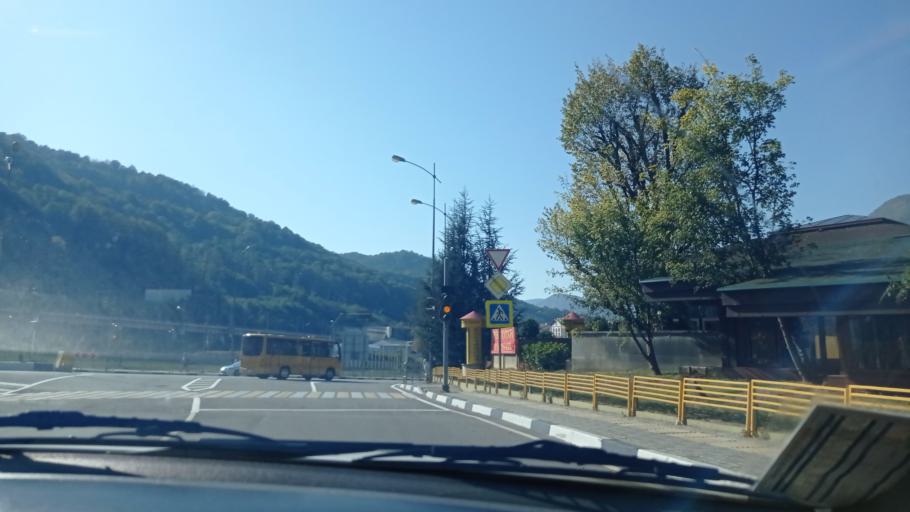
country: RU
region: Krasnodarskiy
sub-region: Sochi City
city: Krasnaya Polyana
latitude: 43.6820
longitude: 40.2748
